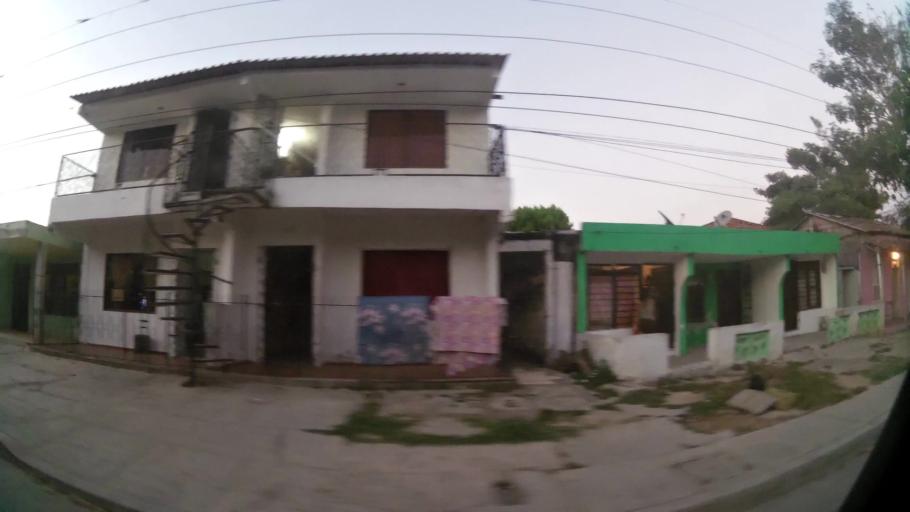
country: CO
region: Bolivar
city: Cartagena
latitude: 10.4133
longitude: -75.5198
